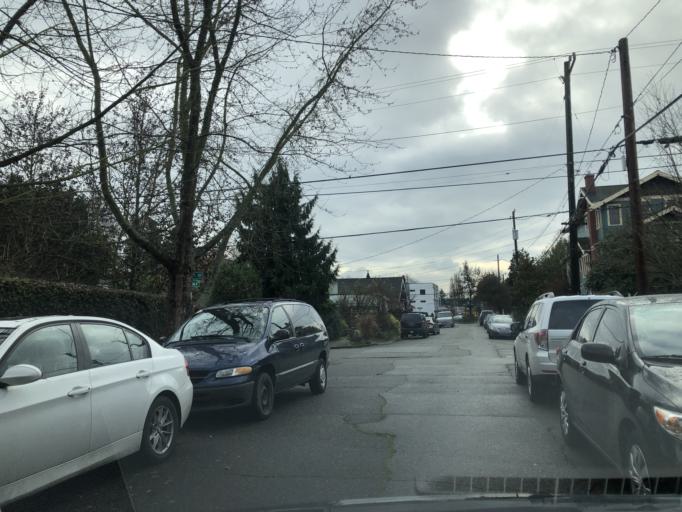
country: US
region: Washington
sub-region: King County
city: Seattle
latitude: 47.6638
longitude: -122.3515
